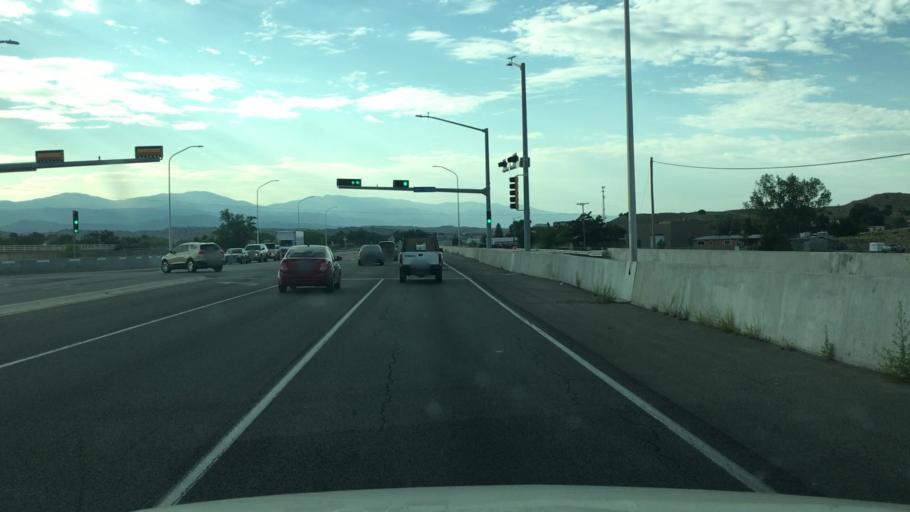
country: US
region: New Mexico
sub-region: Santa Fe County
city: El Valle de Arroyo Seco
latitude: 35.9624
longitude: -106.0293
